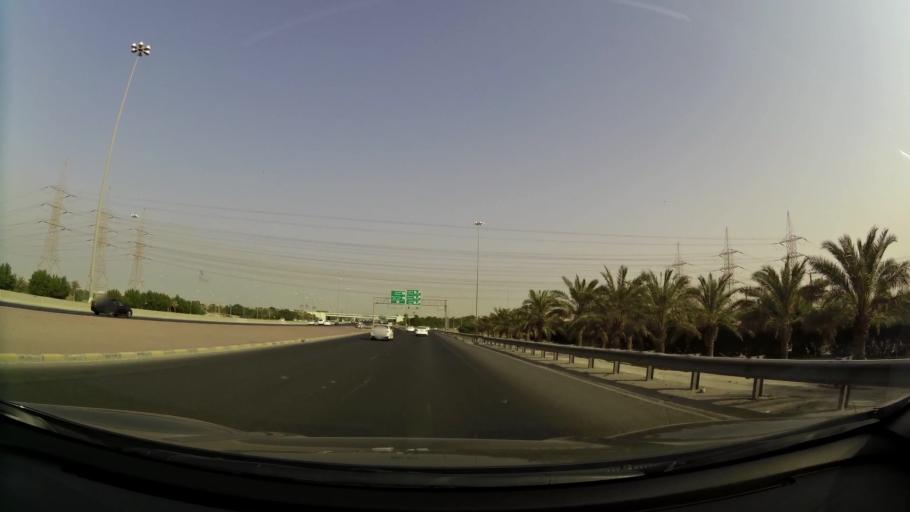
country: KW
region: Muhafazat al Jahra'
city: Al Jahra'
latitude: 29.3115
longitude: 47.7791
